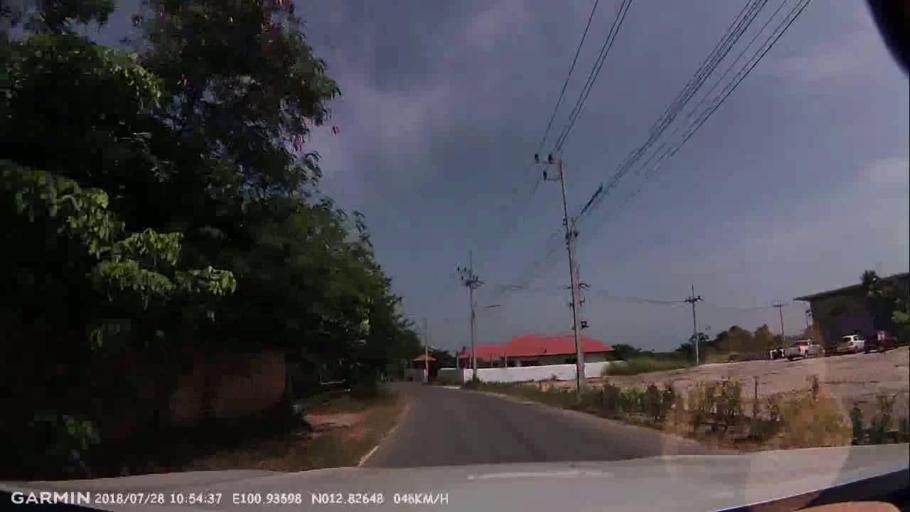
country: TH
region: Chon Buri
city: Phatthaya
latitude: 12.8265
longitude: 100.9359
